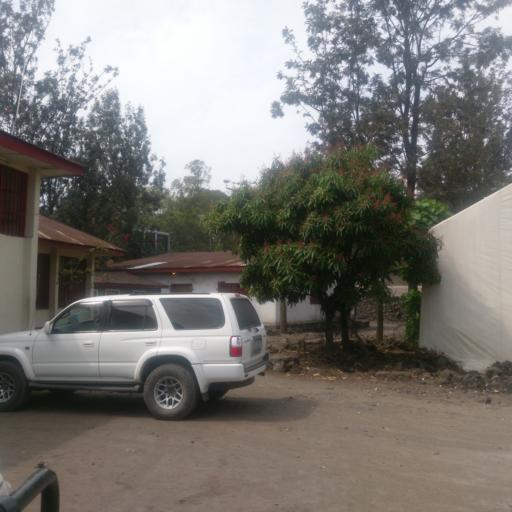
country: CD
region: Nord Kivu
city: Goma
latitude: -1.6789
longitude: 29.2308
